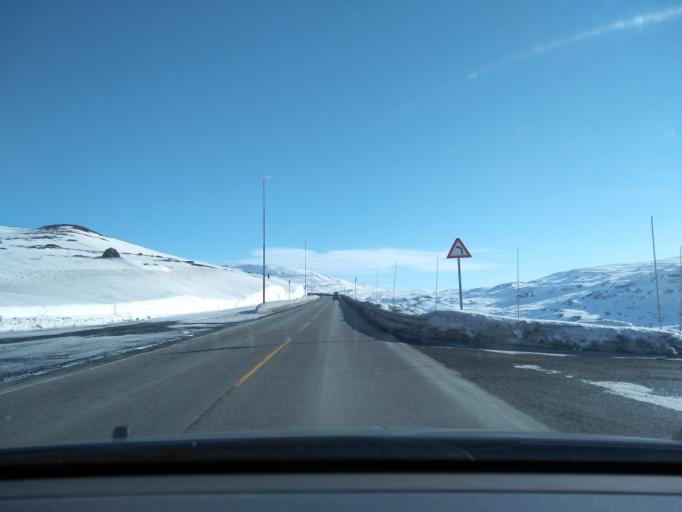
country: NO
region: Aust-Agder
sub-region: Bykle
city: Hovden
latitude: 59.8444
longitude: 6.9732
